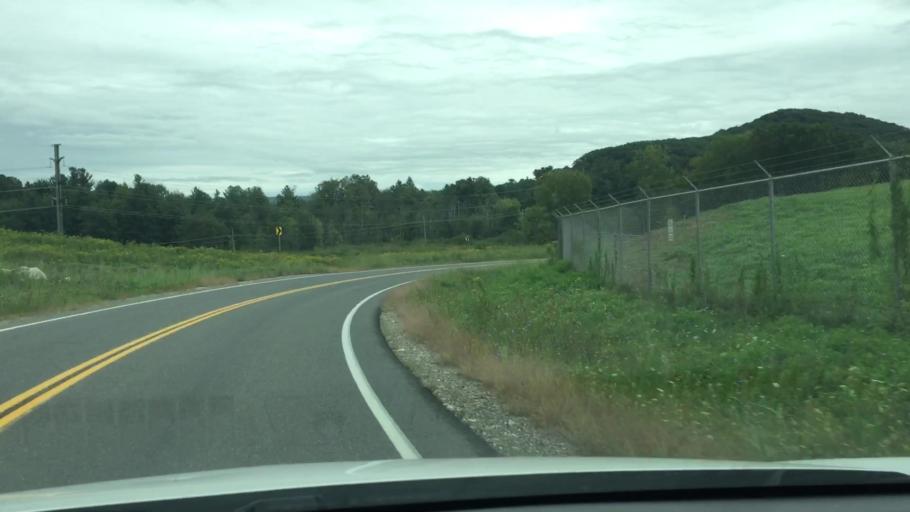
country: US
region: Massachusetts
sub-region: Berkshire County
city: Pittsfield
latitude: 42.4334
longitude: -73.2784
